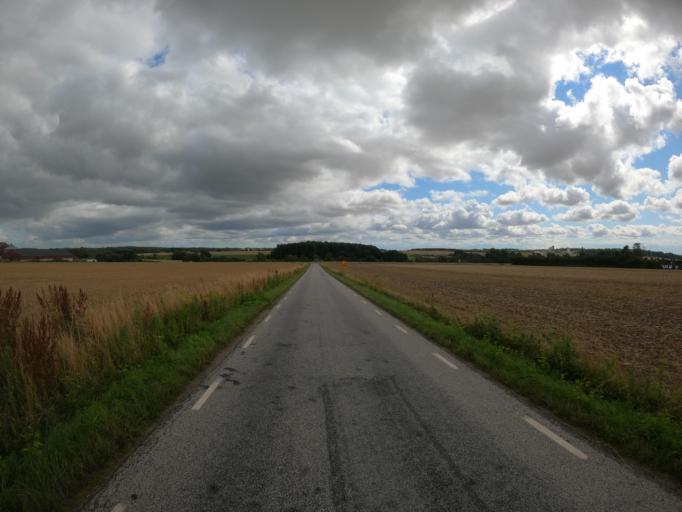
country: SE
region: Skane
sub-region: Lunds Kommun
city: Lund
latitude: 55.7169
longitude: 13.3016
